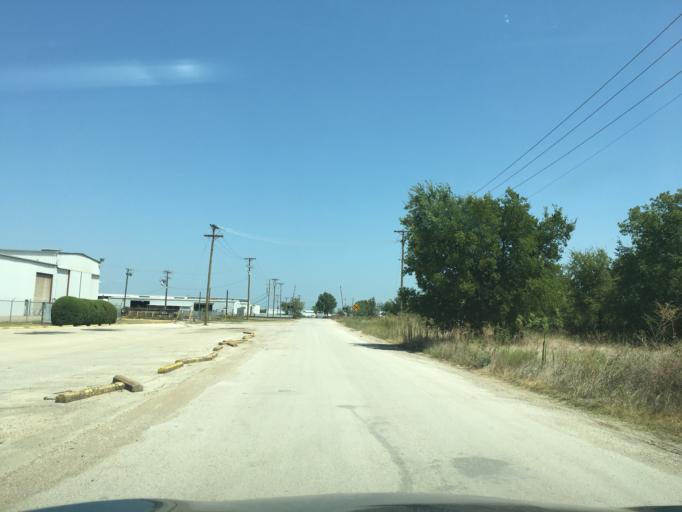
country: US
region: Texas
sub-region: Tarrant County
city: Crowley
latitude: 32.6147
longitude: -97.3564
